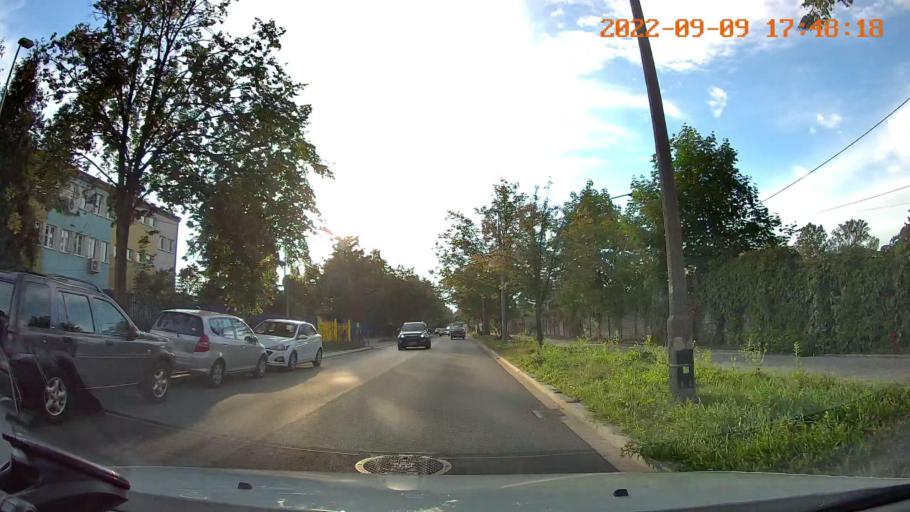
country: PL
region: Lesser Poland Voivodeship
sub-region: Powiat krakowski
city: Rzaska
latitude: 50.0792
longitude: 19.8744
